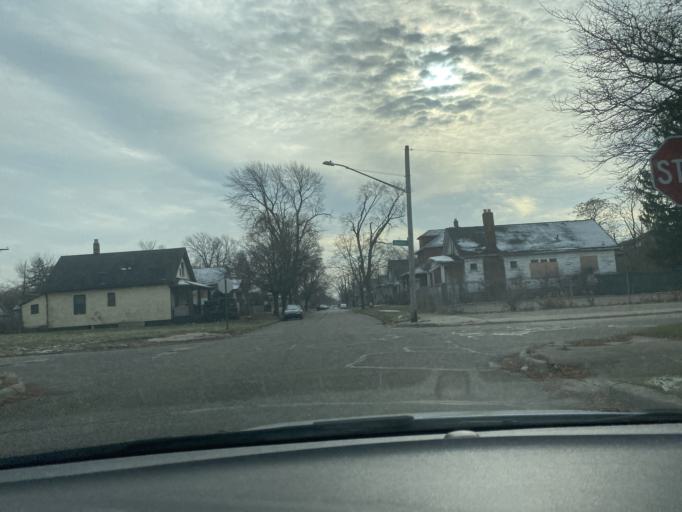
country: US
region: Michigan
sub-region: Wayne County
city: Highland Park
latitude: 42.3708
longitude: -83.1320
